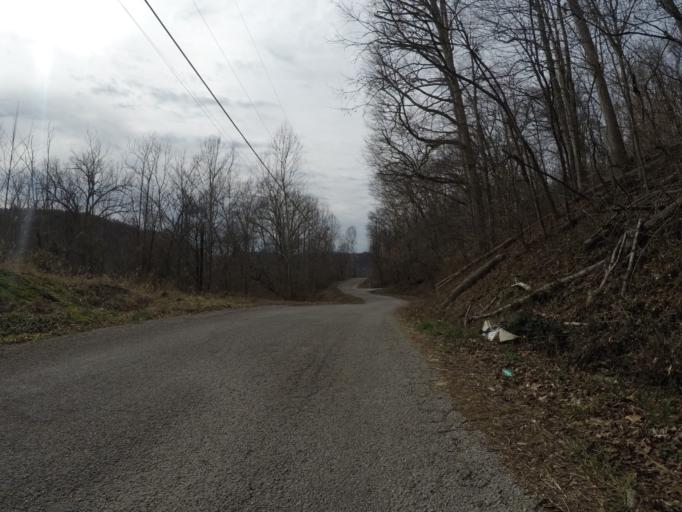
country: US
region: West Virginia
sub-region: Cabell County
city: Huntington
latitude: 38.4435
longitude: -82.4474
